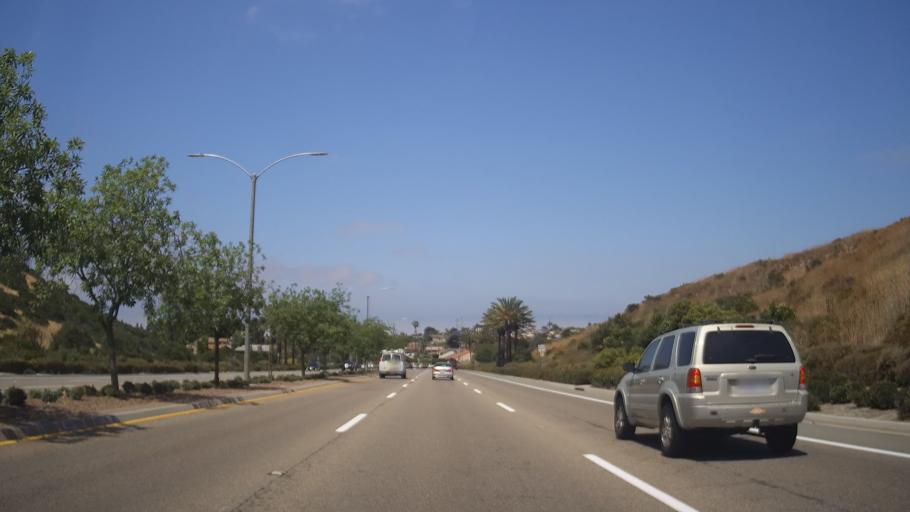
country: US
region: California
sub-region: San Diego County
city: Bonita
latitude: 32.6090
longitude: -117.0245
